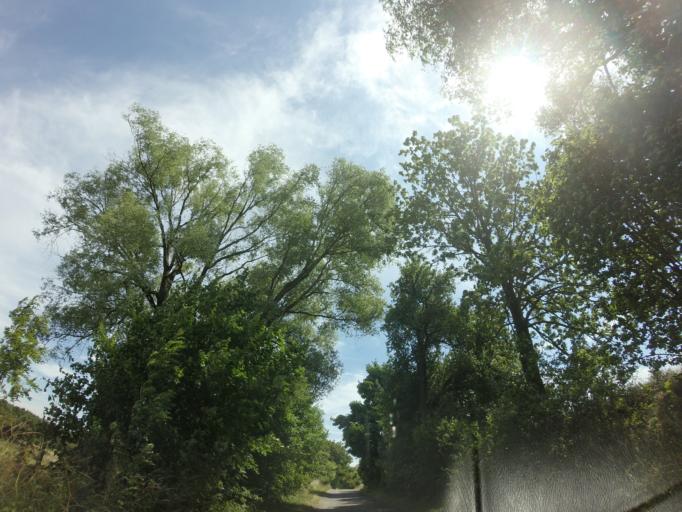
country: PL
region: West Pomeranian Voivodeship
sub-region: Powiat choszczenski
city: Recz
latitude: 53.3401
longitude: 15.5582
